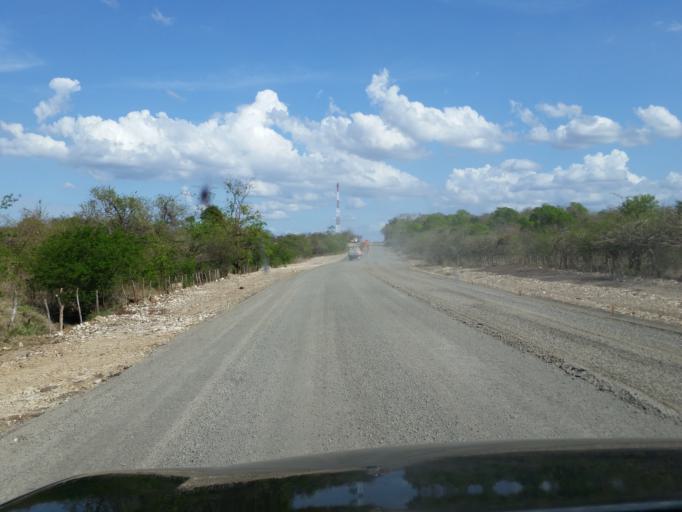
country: NI
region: Leon
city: Nagarote
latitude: 12.1774
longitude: -86.6683
